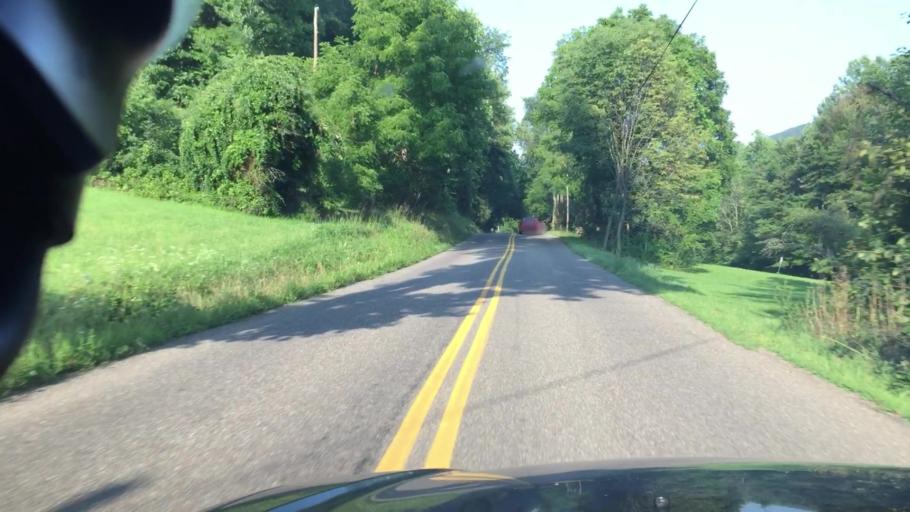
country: US
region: Pennsylvania
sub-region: Columbia County
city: Espy
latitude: 40.9719
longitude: -76.4122
